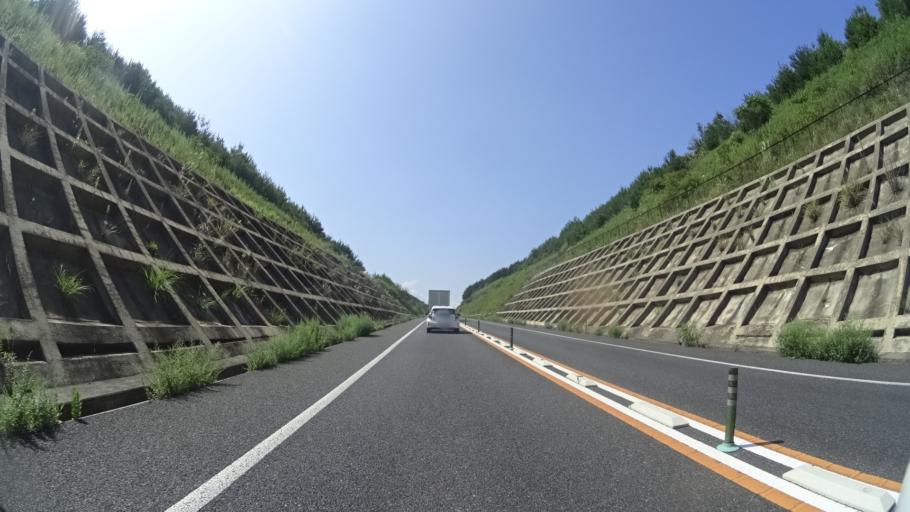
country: JP
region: Shimane
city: Masuda
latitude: 34.7042
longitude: 131.8579
